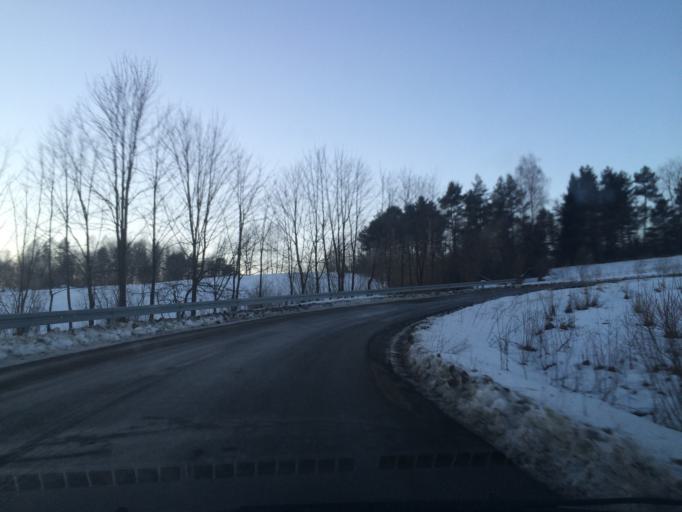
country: PL
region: Subcarpathian Voivodeship
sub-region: Powiat bieszczadzki
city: Czarna
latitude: 49.3859
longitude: 22.6342
